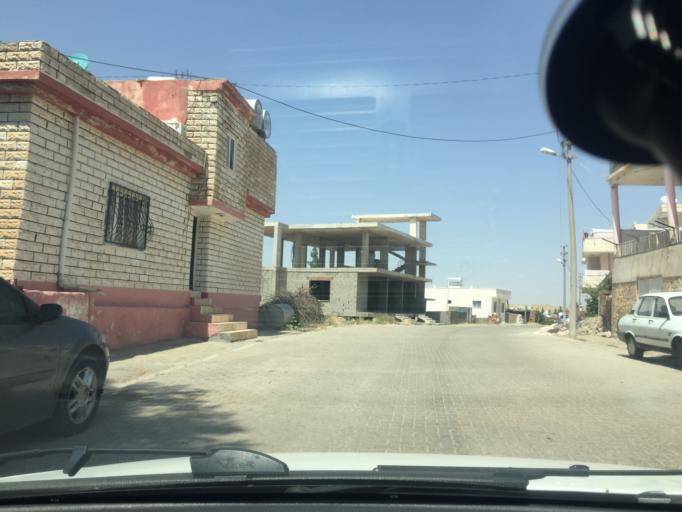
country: TR
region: Mardin
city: Kindirip
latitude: 37.4514
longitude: 41.2227
